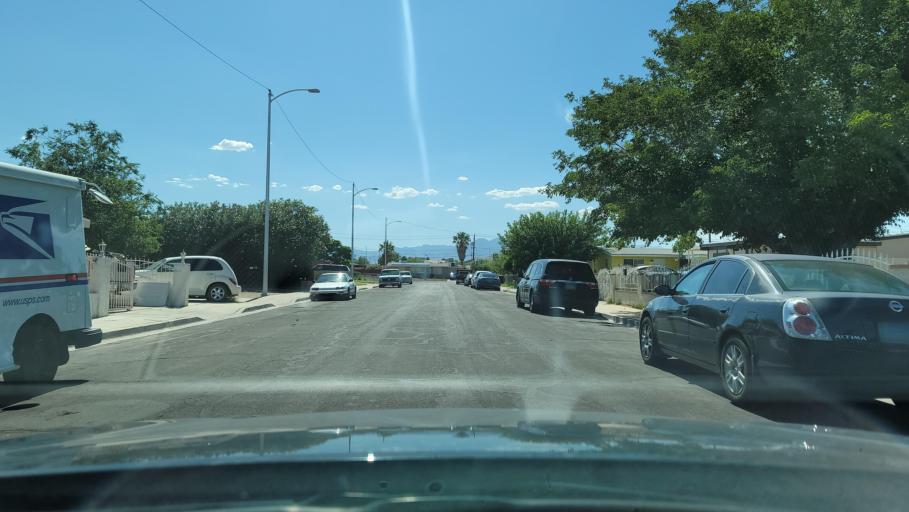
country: US
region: Nevada
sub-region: Clark County
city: Las Vegas
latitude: 36.1924
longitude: -115.1497
